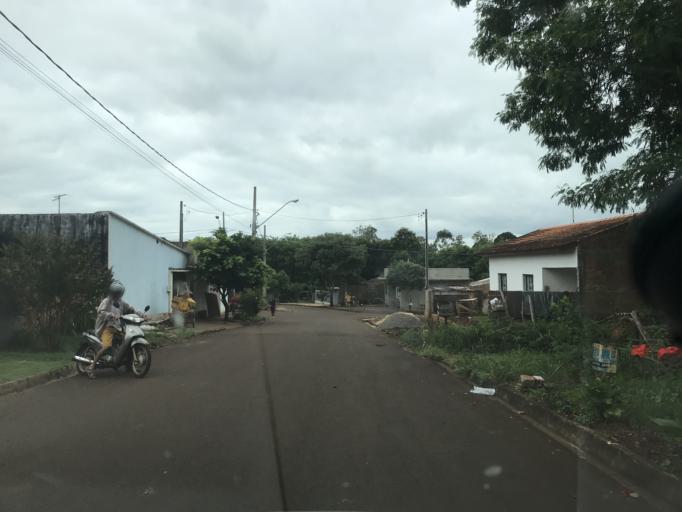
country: BR
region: Parana
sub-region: Palotina
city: Palotina
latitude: -24.3001
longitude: -53.8295
